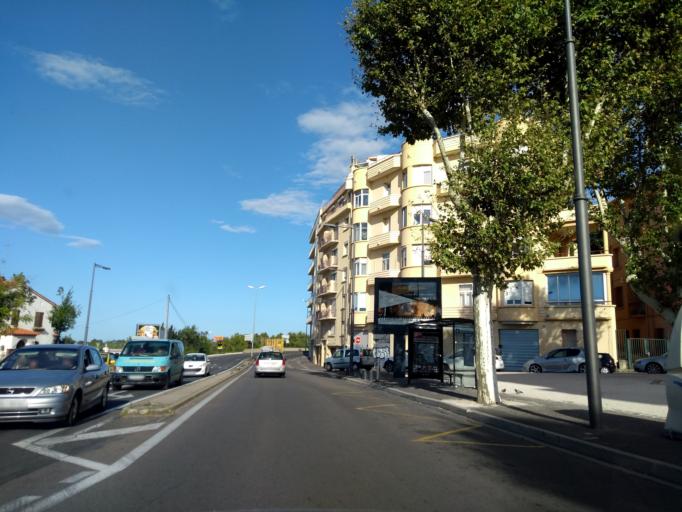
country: FR
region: Languedoc-Roussillon
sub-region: Departement des Pyrenees-Orientales
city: Perpignan
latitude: 42.6987
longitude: 2.9054
